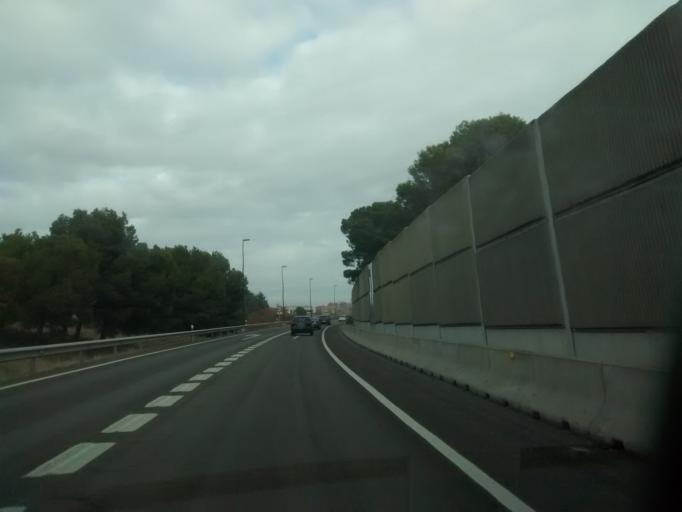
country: ES
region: Aragon
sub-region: Provincia de Zaragoza
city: Zaragoza
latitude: 41.6771
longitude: -0.8785
